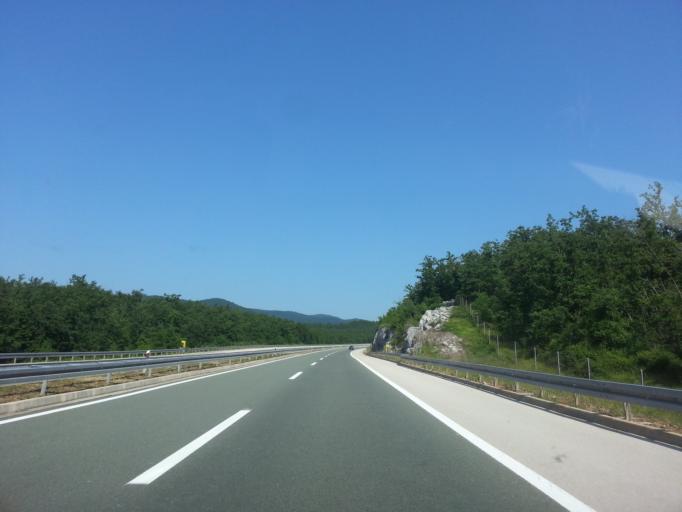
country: HR
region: Primorsko-Goranska
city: Matulji
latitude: 45.4335
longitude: 14.2839
